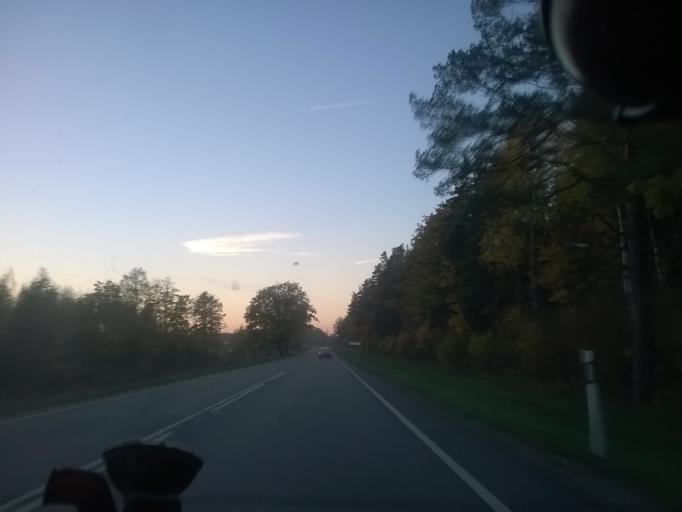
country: EE
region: Laeaene
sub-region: Ridala Parish
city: Uuemoisa
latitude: 58.9579
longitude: 23.7202
